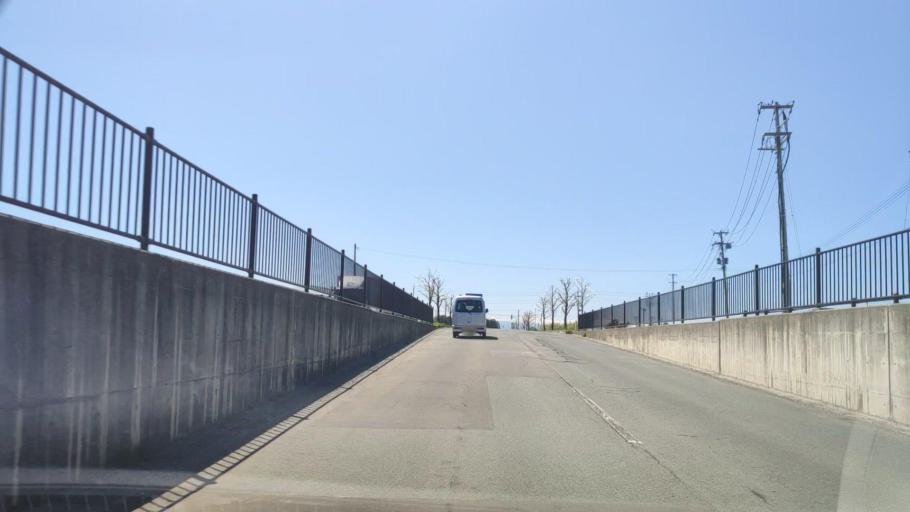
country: JP
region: Yamagata
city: Tendo
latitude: 38.3736
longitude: 140.3713
